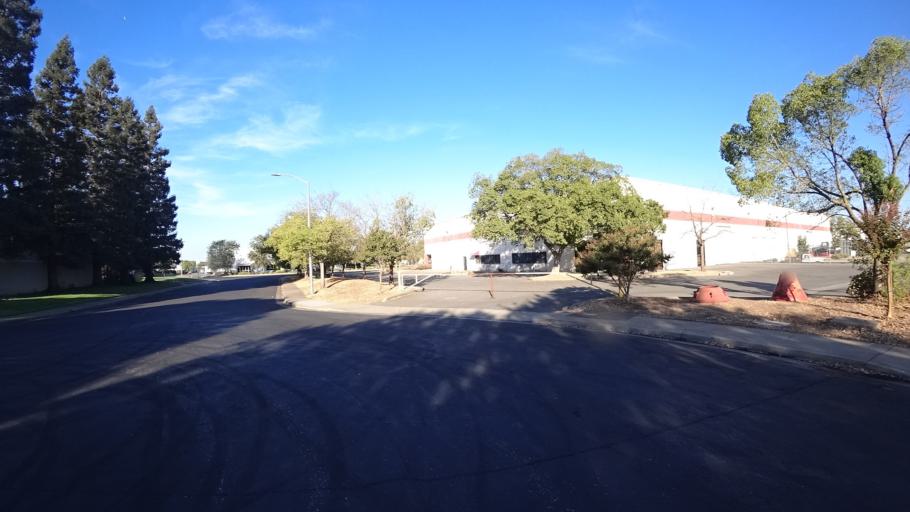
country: US
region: California
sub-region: Sacramento County
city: Florin
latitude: 38.5146
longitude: -121.3836
